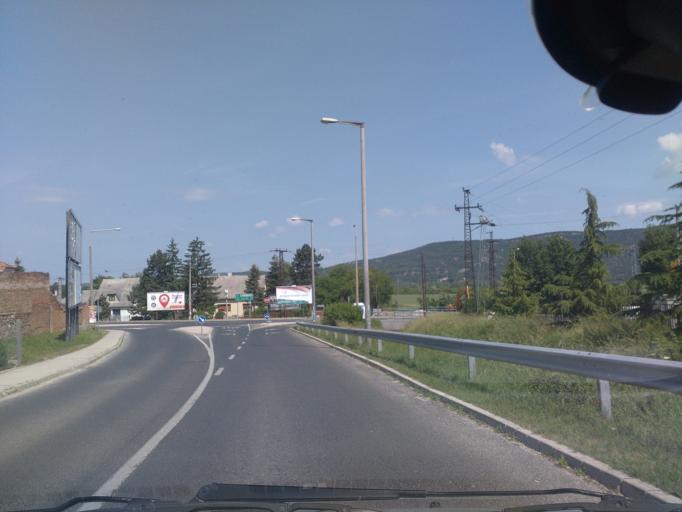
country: HU
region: Komarom-Esztergom
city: Esztergom
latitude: 47.8035
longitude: 18.7511
